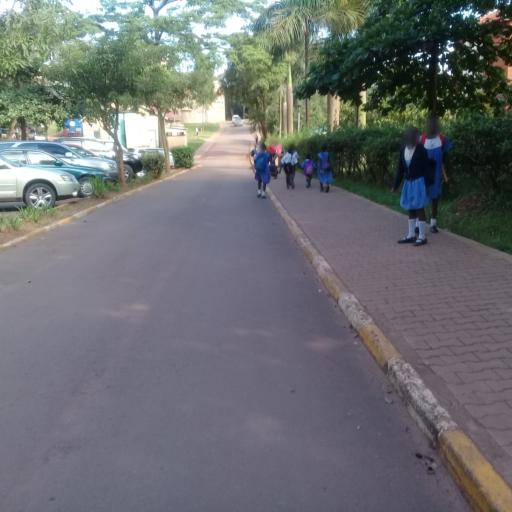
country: UG
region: Central Region
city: Kampala Central Division
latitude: 0.3367
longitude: 32.5649
